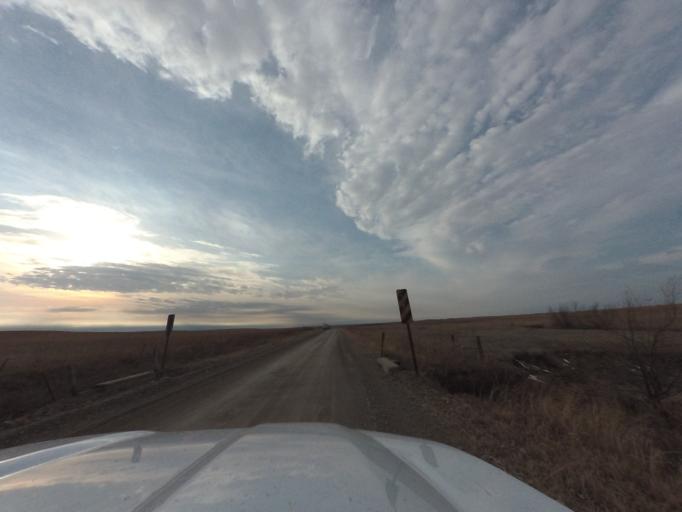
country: US
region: Kansas
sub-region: Morris County
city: Council Grove
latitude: 38.4989
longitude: -96.4102
